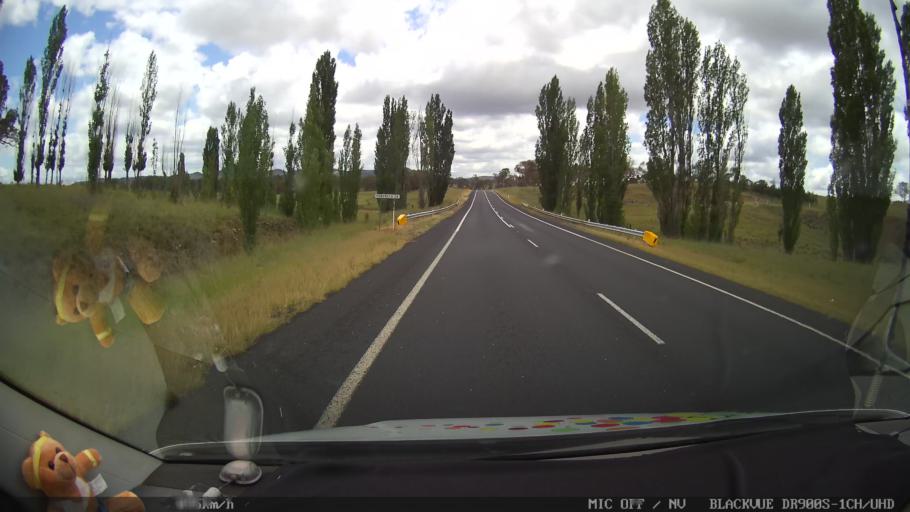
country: AU
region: New South Wales
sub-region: Glen Innes Severn
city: Glen Innes
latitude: -29.3896
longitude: 151.8863
